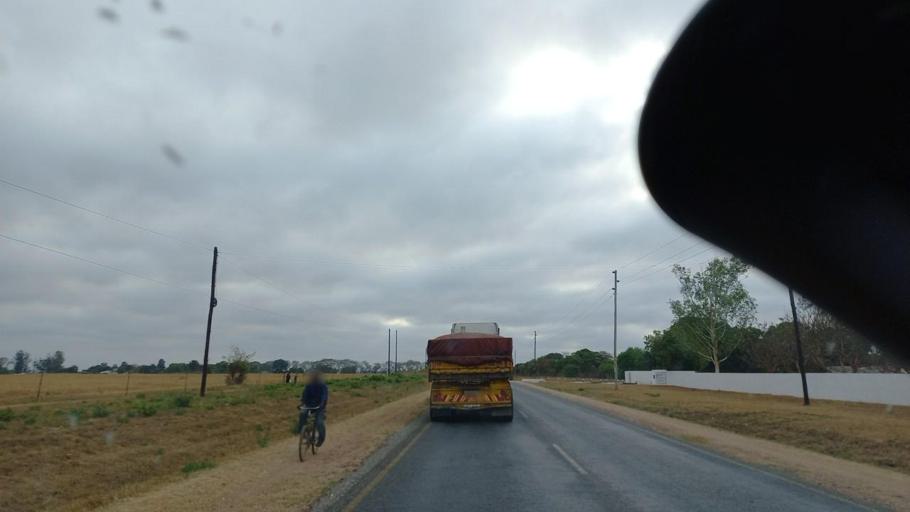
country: ZM
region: Lusaka
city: Chongwe
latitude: -15.3504
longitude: 28.5619
